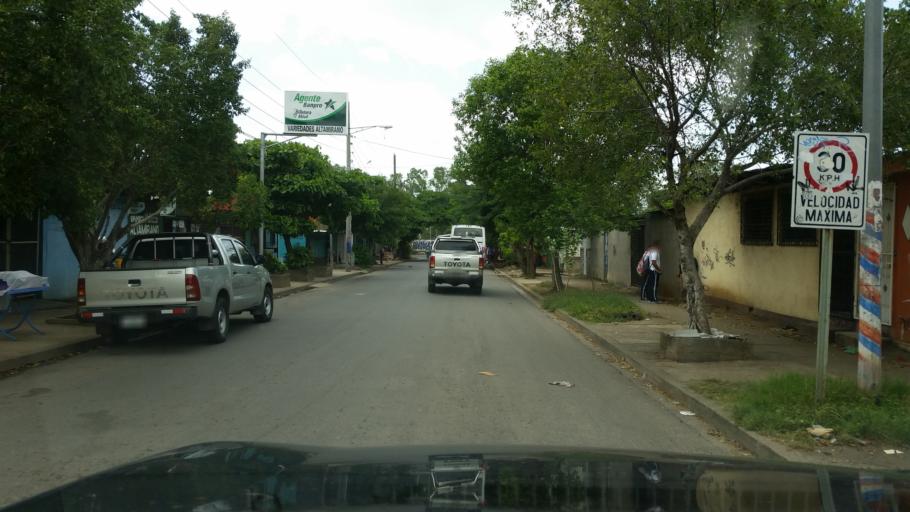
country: NI
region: Managua
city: Managua
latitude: 12.1383
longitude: -86.2091
